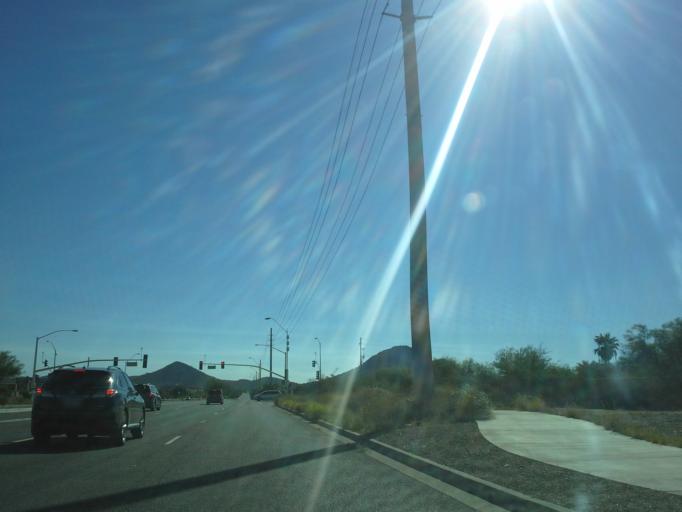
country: US
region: Arizona
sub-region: Maricopa County
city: Fountain Hills
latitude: 33.5823
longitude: -111.8147
